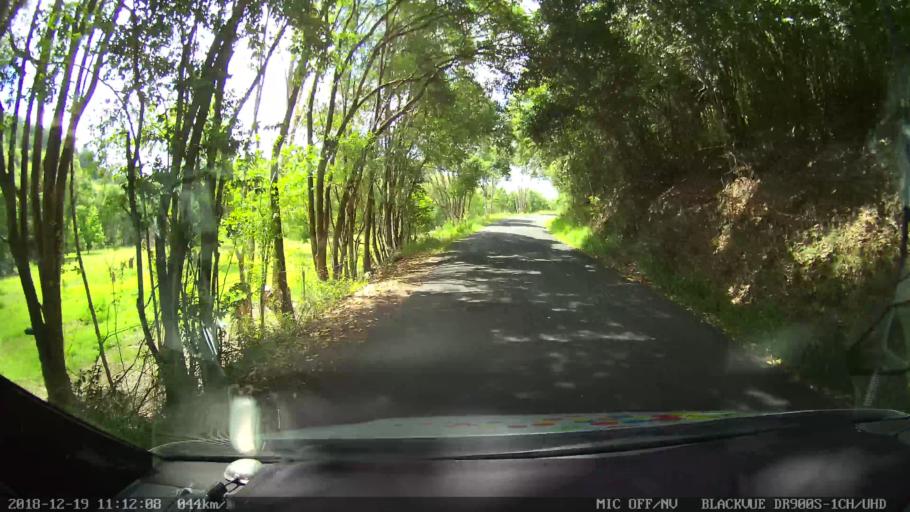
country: AU
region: New South Wales
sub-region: Lismore Municipality
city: Nimbin
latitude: -28.6470
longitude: 153.2603
